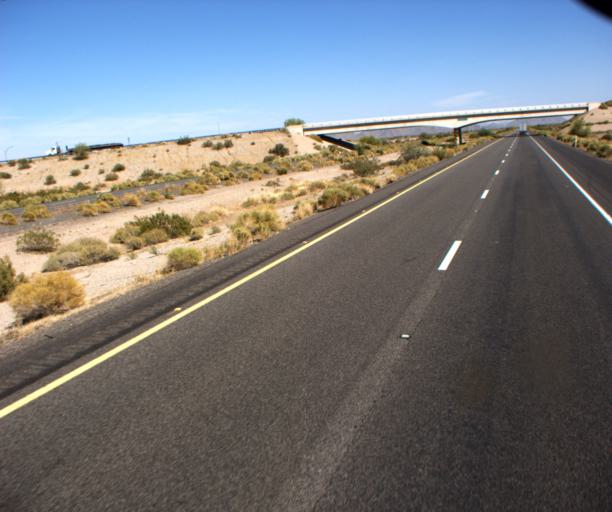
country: US
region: Arizona
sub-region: Maricopa County
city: Gila Bend
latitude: 32.9256
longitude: -112.6733
